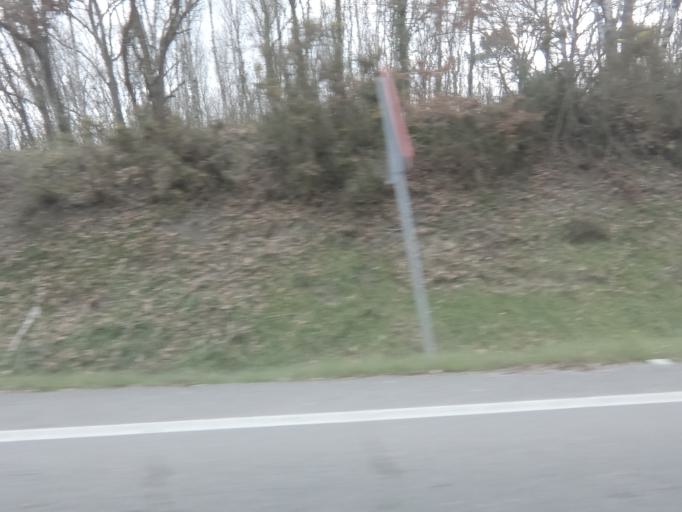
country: ES
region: Galicia
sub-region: Provincia de Ourense
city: Allariz
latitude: 42.2003
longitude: -7.8057
